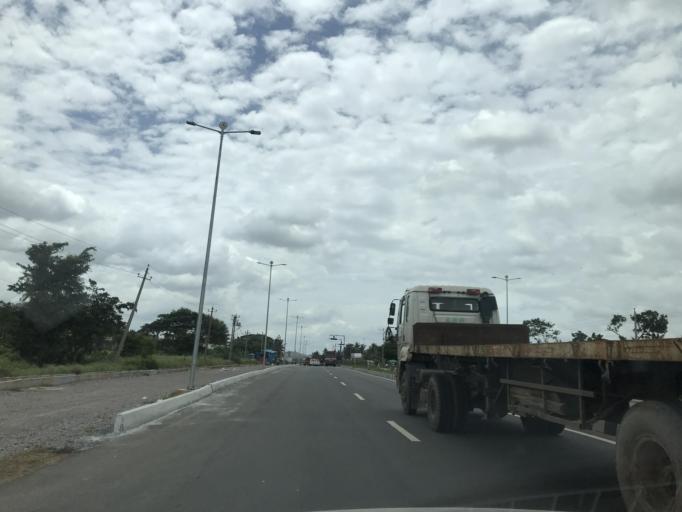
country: IN
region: Karnataka
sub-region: Tumkur
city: Tumkur
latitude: 13.3091
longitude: 77.1411
